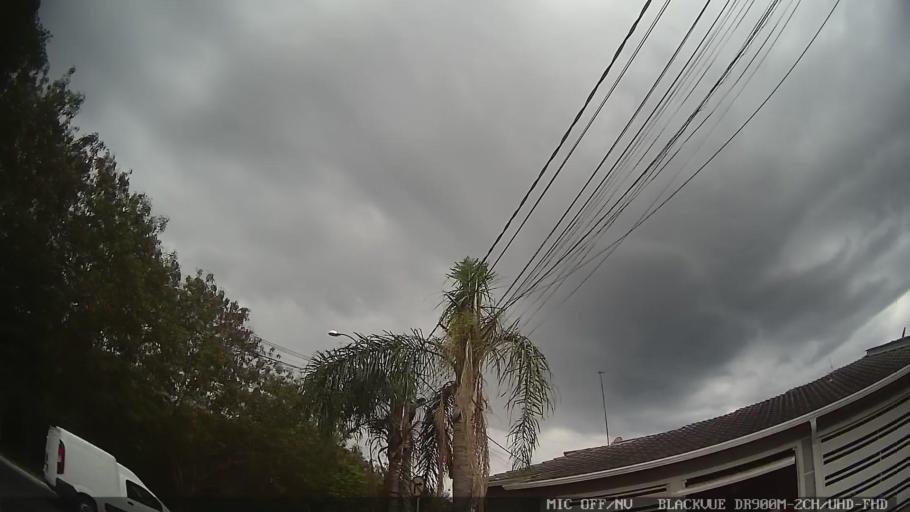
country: BR
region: Sao Paulo
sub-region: Amparo
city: Amparo
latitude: -22.7099
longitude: -46.8084
